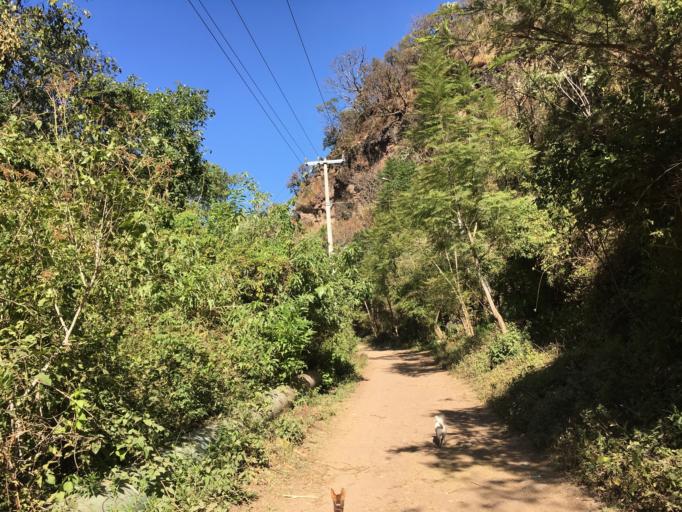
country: MX
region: Michoacan
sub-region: Morelia
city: Montana Monarca (Punta Altozano)
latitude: 19.6775
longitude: -101.1551
